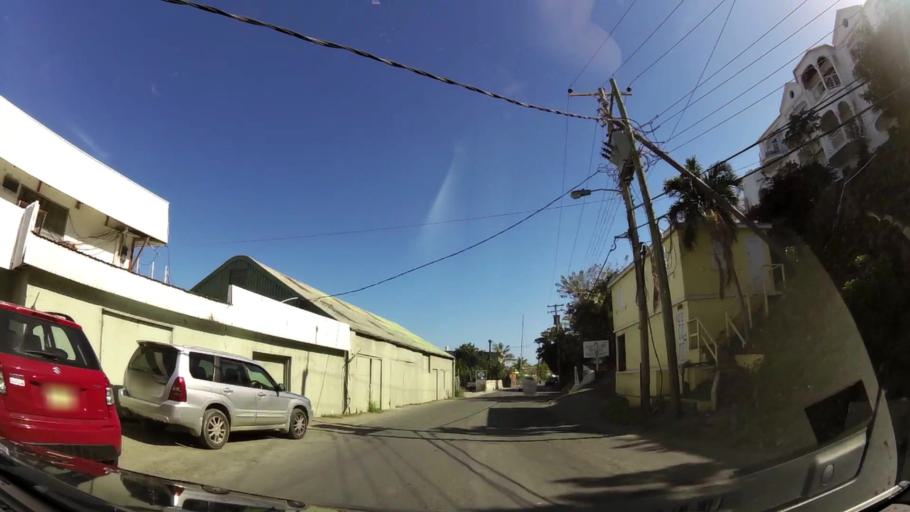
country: VG
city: Road Town
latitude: 18.4137
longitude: -64.6148
